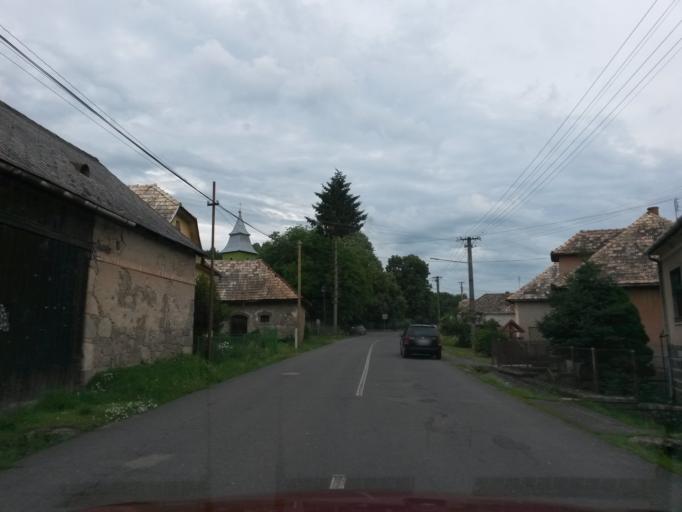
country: SK
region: Banskobystricky
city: Velky Krtis
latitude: 48.2996
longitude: 19.4012
